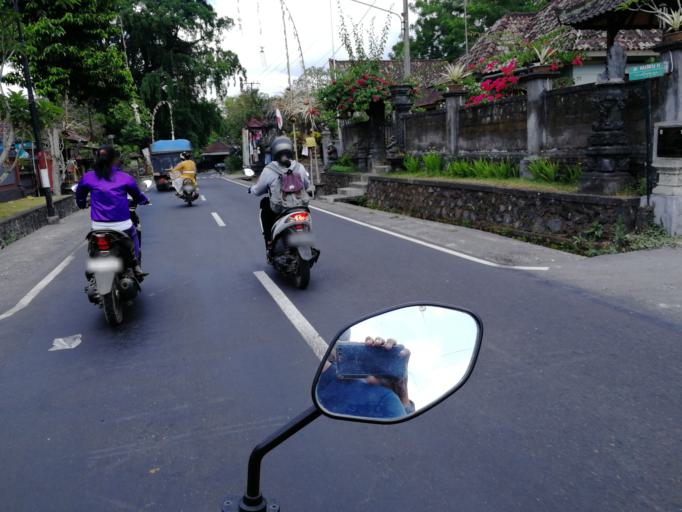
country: ID
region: Bali
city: Banjar Kubu
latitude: -8.4286
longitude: 115.4194
